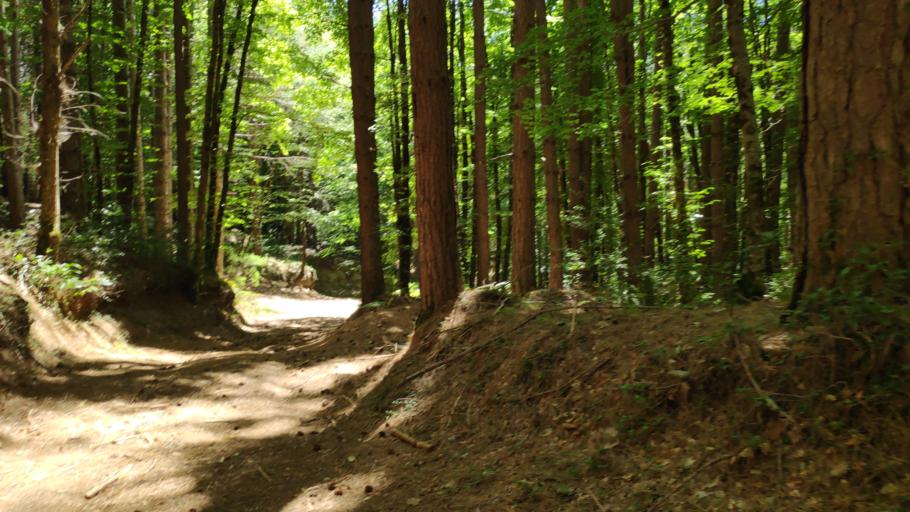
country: IT
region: Calabria
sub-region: Provincia di Vibo-Valentia
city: Nardodipace
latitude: 38.5056
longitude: 16.3732
